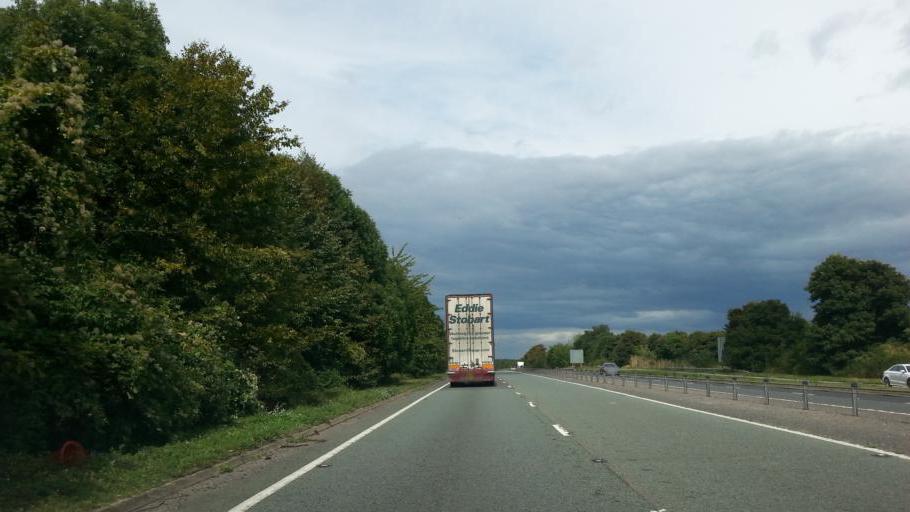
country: GB
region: England
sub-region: Cambridgeshire
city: Sawston
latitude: 52.1020
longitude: 0.2083
